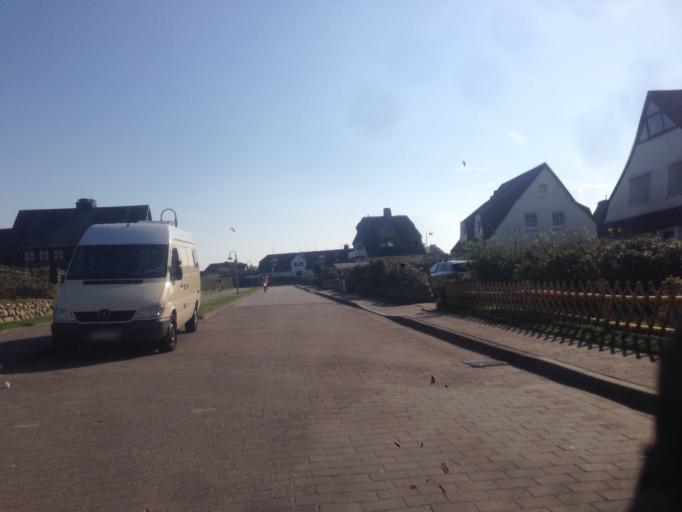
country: DE
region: Schleswig-Holstein
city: Westerland
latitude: 54.9350
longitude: 8.3164
